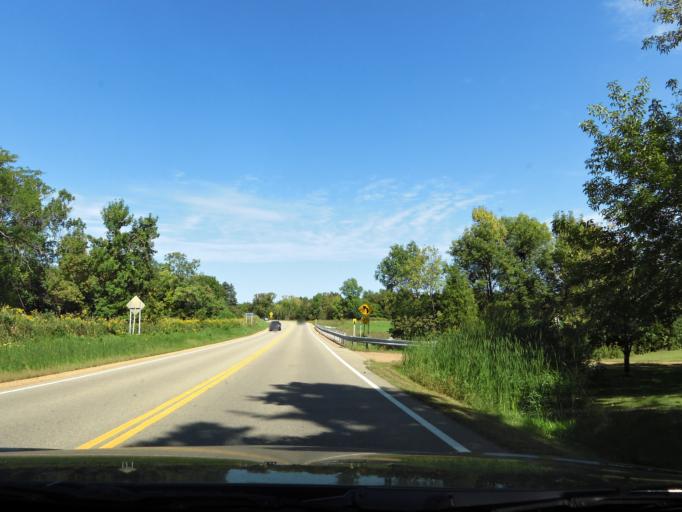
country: US
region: Minnesota
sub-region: Scott County
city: Shakopee
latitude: 44.8201
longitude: -93.5376
